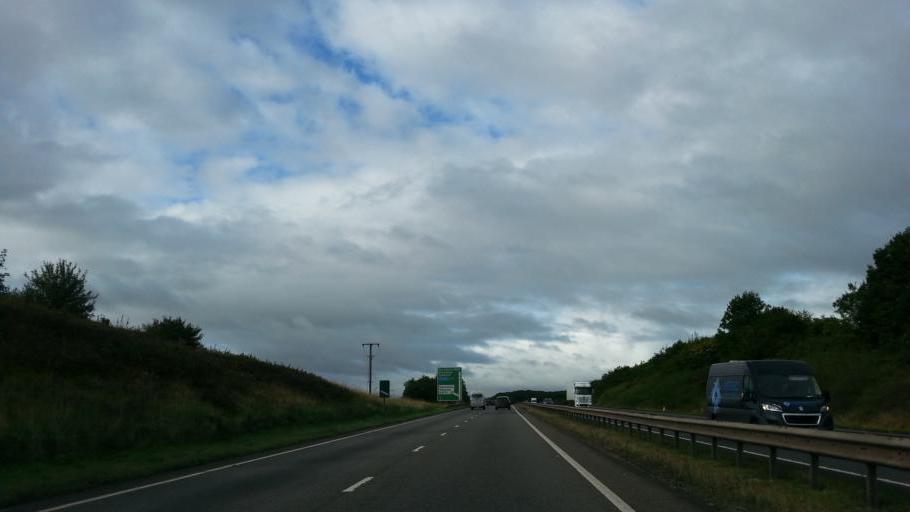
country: GB
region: England
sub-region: Leicestershire
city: Ashby de la Zouch
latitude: 52.7293
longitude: -1.4800
